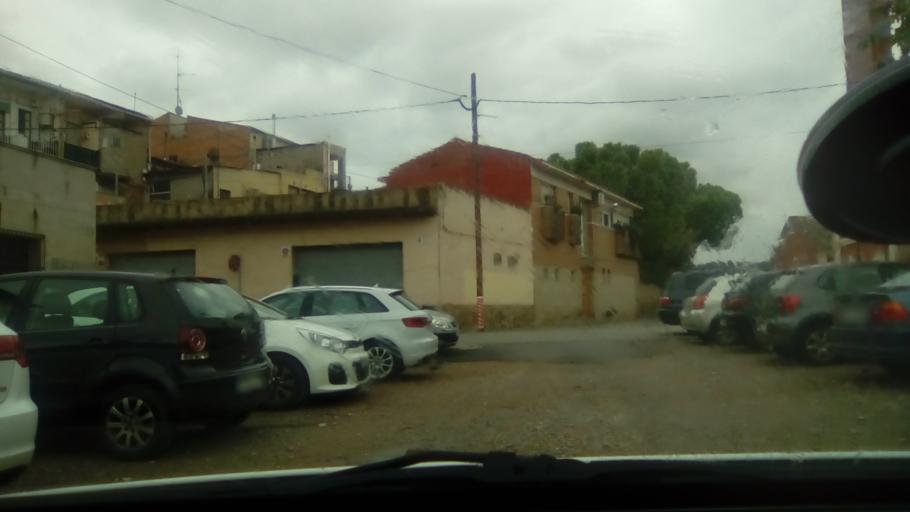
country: ES
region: Catalonia
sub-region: Provincia de Barcelona
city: Monistrol de Montserrat
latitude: 41.6690
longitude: 1.8628
